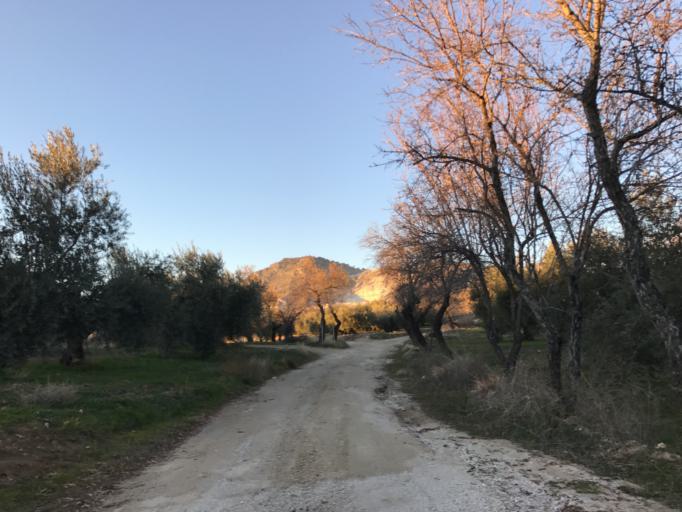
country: ES
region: Andalusia
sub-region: Provincia de Granada
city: Beas de Granada
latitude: 37.2235
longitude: -3.4728
